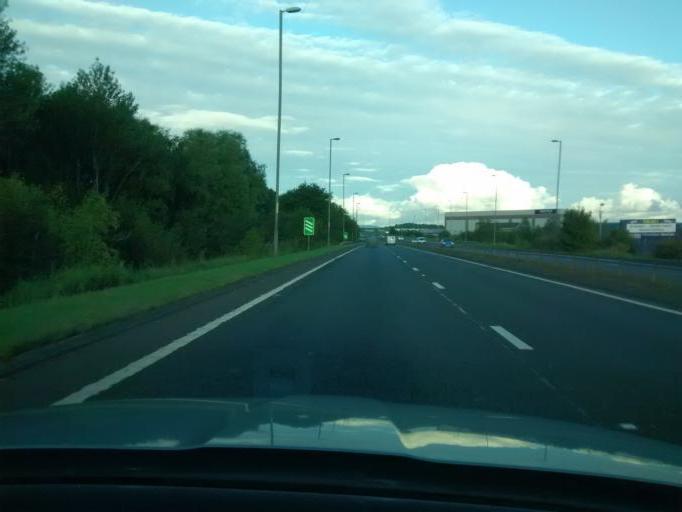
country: GB
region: Scotland
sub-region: Renfrewshire
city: Elderslie
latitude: 55.8440
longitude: -4.4932
